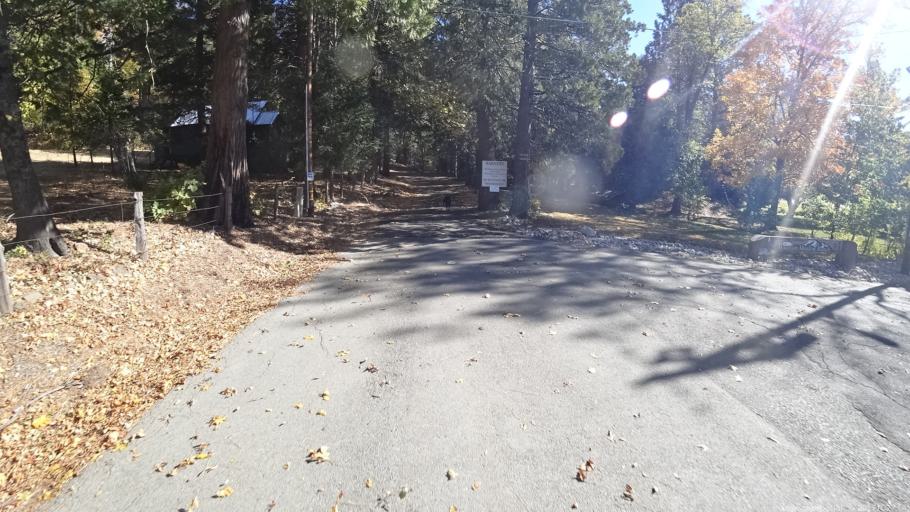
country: US
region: California
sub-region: Shasta County
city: Burney
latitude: 40.8055
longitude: -121.8910
